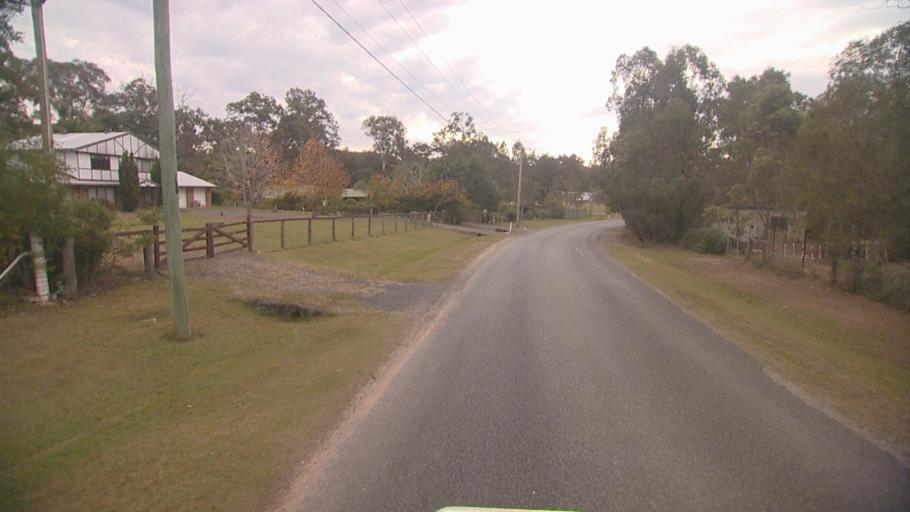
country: AU
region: Queensland
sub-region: Logan
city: Chambers Flat
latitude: -27.7918
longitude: 153.1161
